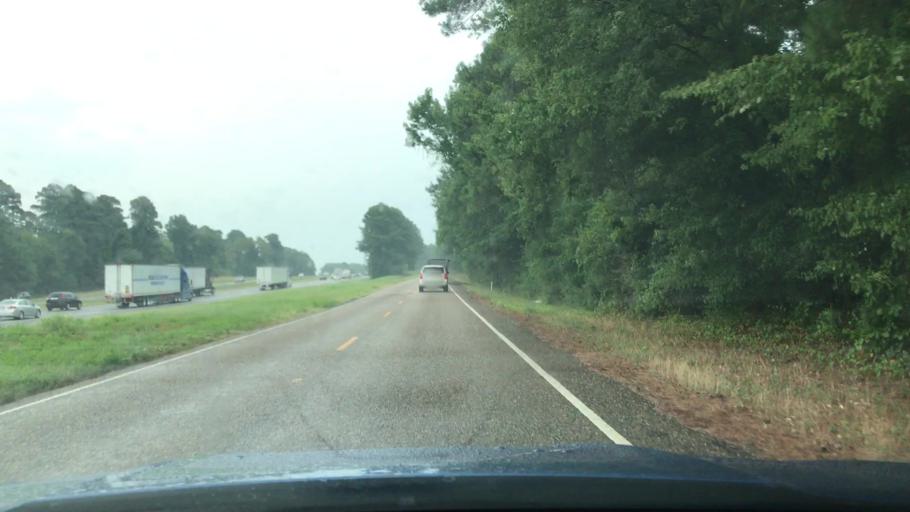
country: US
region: Texas
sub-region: Harrison County
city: Waskom
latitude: 32.4851
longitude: -94.1225
